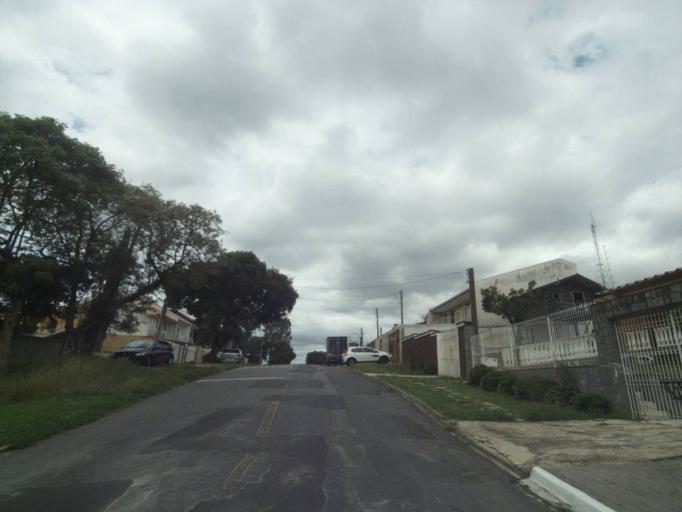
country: BR
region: Parana
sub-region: Curitiba
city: Curitiba
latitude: -25.3928
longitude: -49.2853
